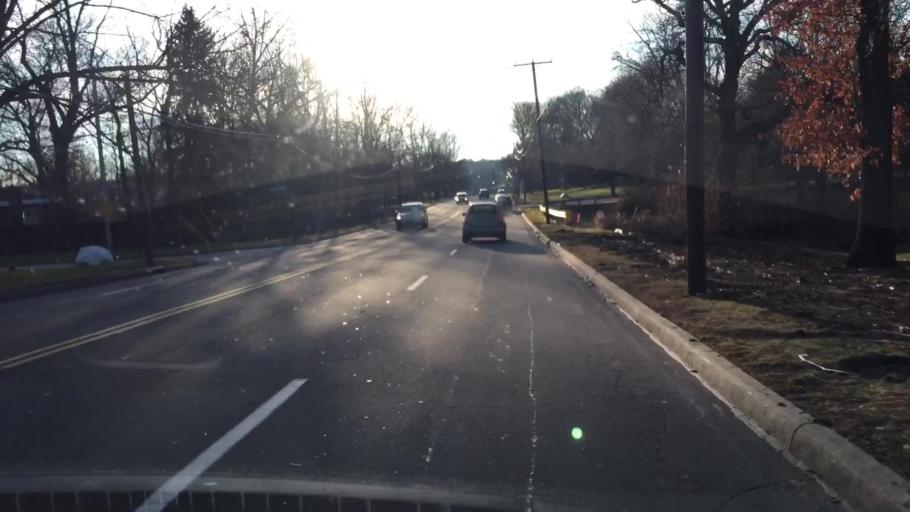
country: US
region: Ohio
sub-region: Summit County
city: Silver Lake
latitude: 41.1563
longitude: -81.4482
